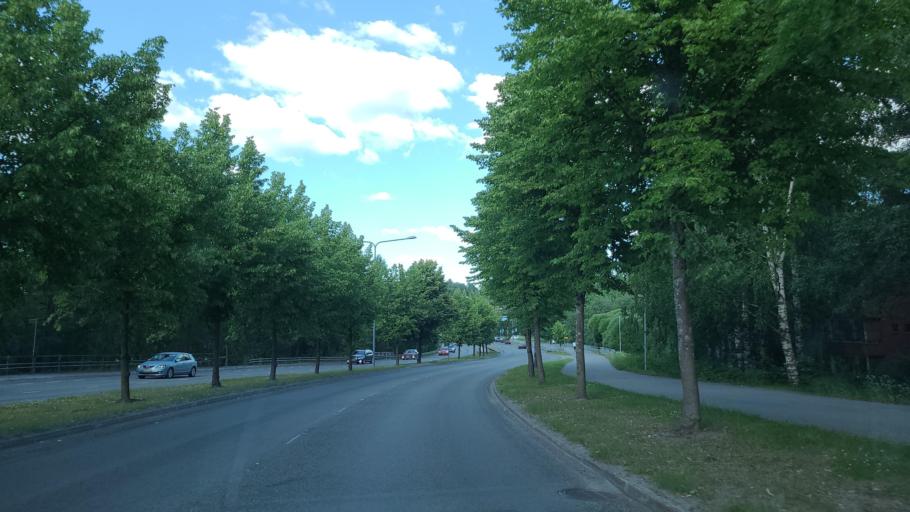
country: FI
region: Central Finland
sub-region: Jyvaeskylae
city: Jyvaeskylae
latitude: 62.2554
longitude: 25.7517
